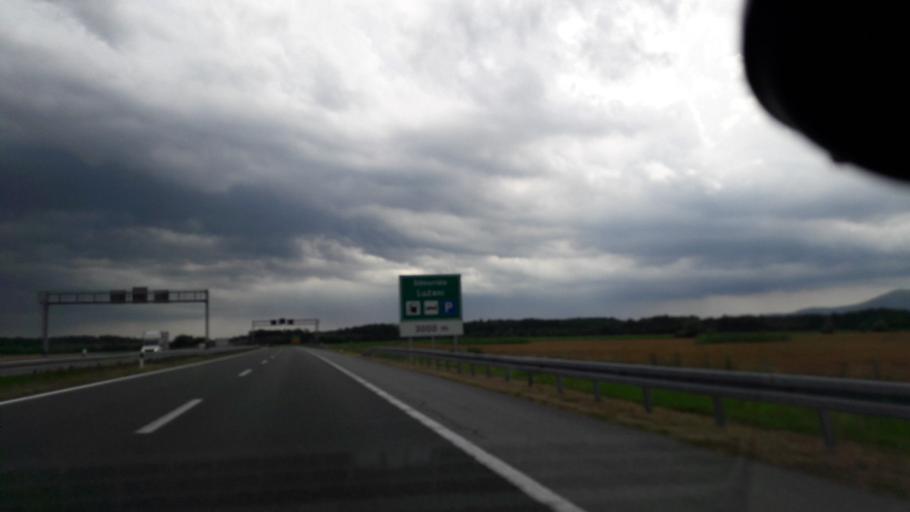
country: HR
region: Brodsko-Posavska
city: Batrina
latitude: 45.1718
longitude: 17.6612
